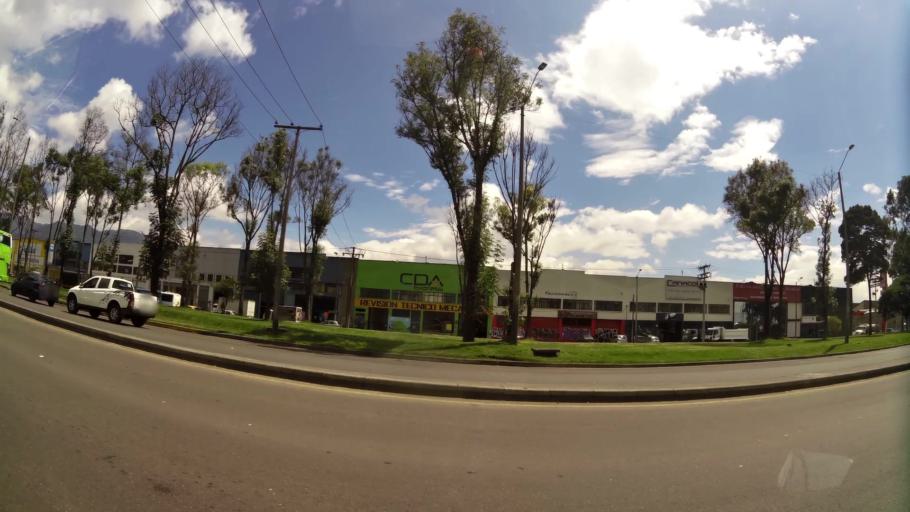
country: CO
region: Bogota D.C.
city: Bogota
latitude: 4.6259
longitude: -74.0929
